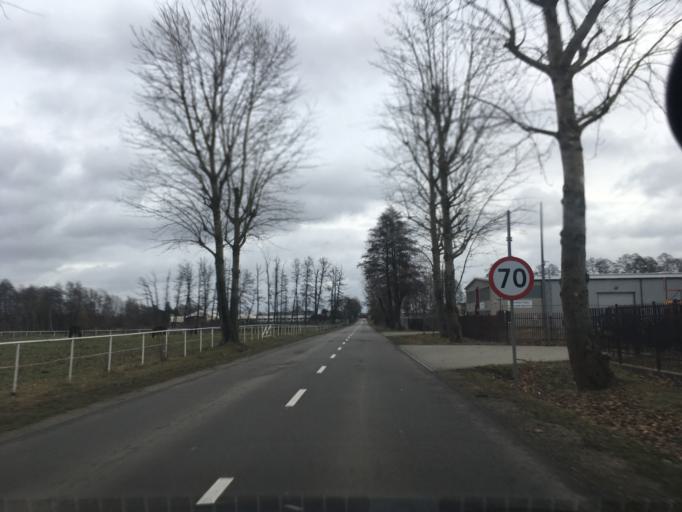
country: PL
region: Masovian Voivodeship
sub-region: Powiat piaseczynski
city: Lesznowola
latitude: 52.1210
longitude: 20.9355
